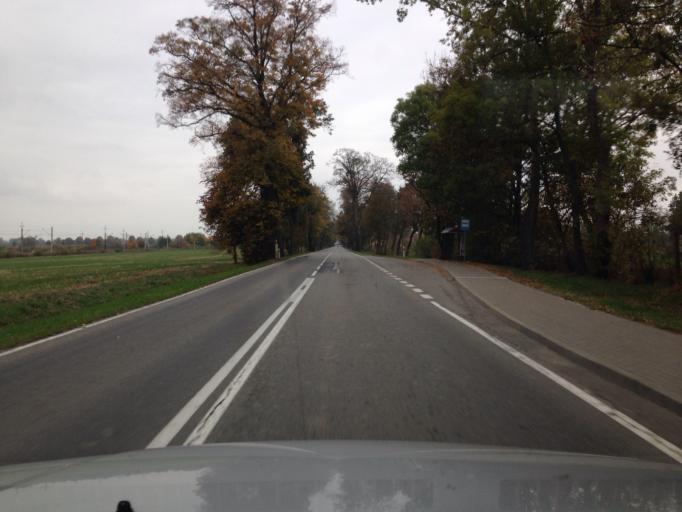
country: PL
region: Pomeranian Voivodeship
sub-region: Powiat malborski
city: Stare Pole
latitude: 54.0453
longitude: 19.1603
